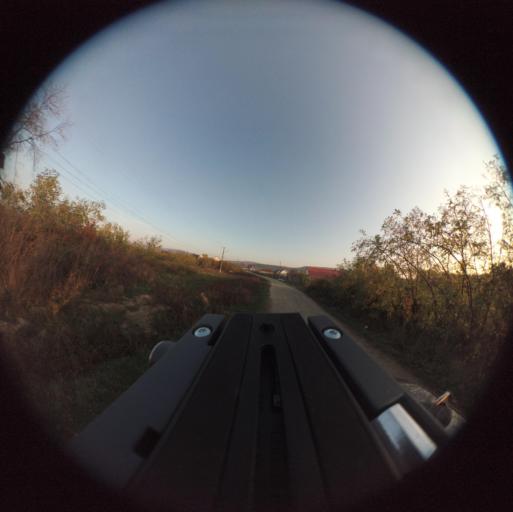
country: RO
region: Vaslui
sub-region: Comuna Bacesti
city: Bacesti
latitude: 46.8290
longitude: 27.2487
